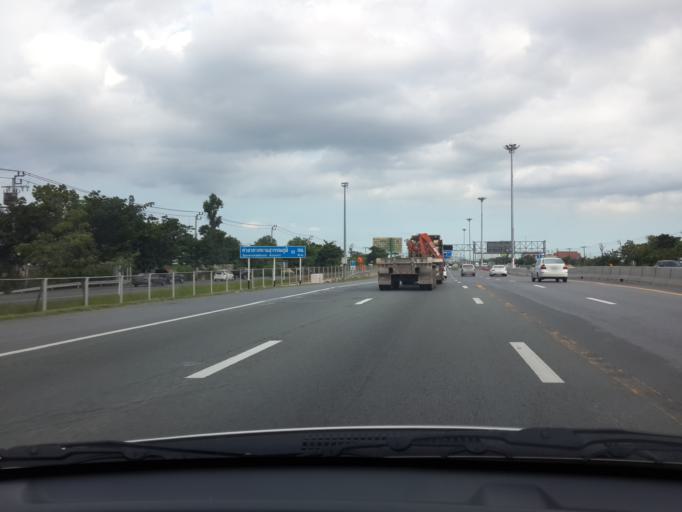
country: TH
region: Bangkok
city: Saphan Sung
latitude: 13.7670
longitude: 100.6932
